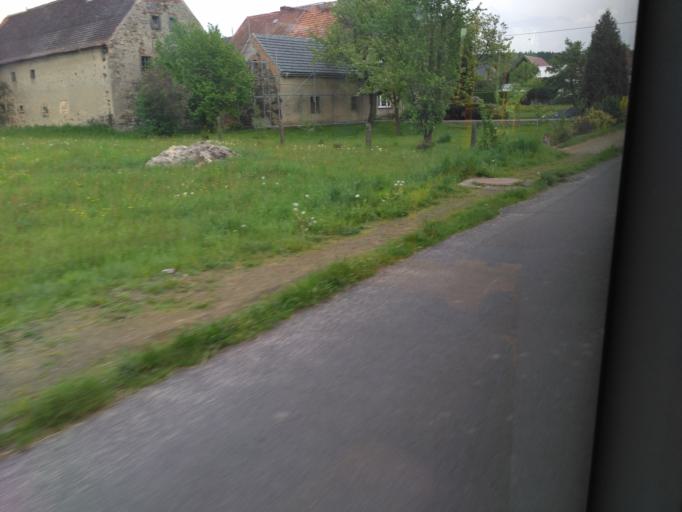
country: DE
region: Saxony
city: Konigsbruck
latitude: 51.2829
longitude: 13.9271
